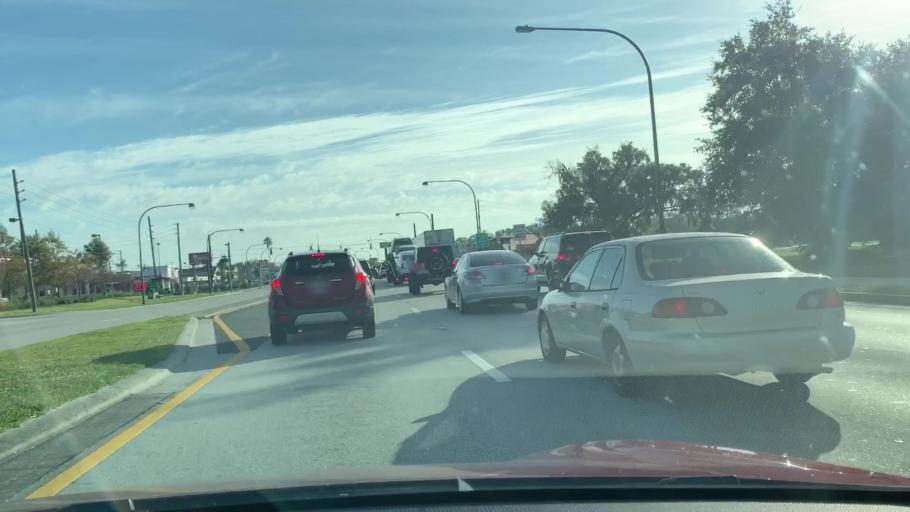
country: US
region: Florida
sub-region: Osceola County
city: Kissimmee
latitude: 28.3045
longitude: -81.4258
